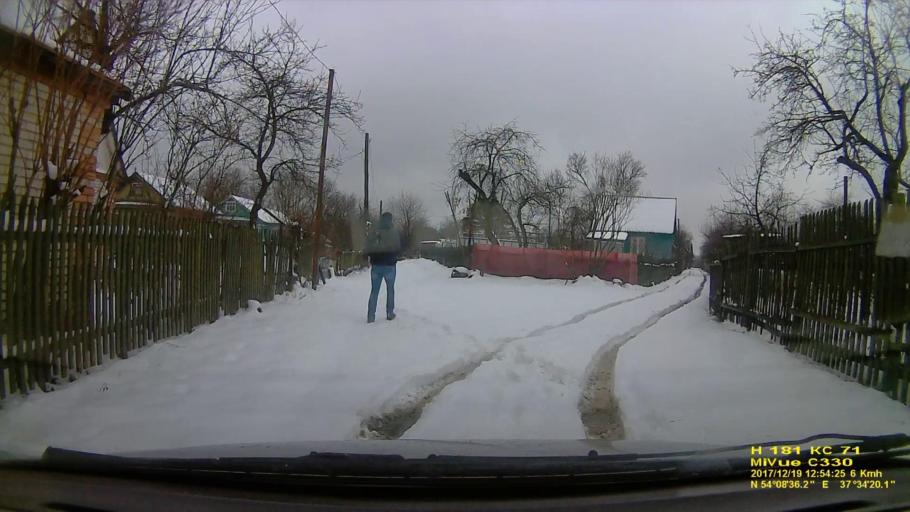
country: RU
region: Tula
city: Mendeleyevskiy
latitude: 54.1434
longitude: 37.5722
